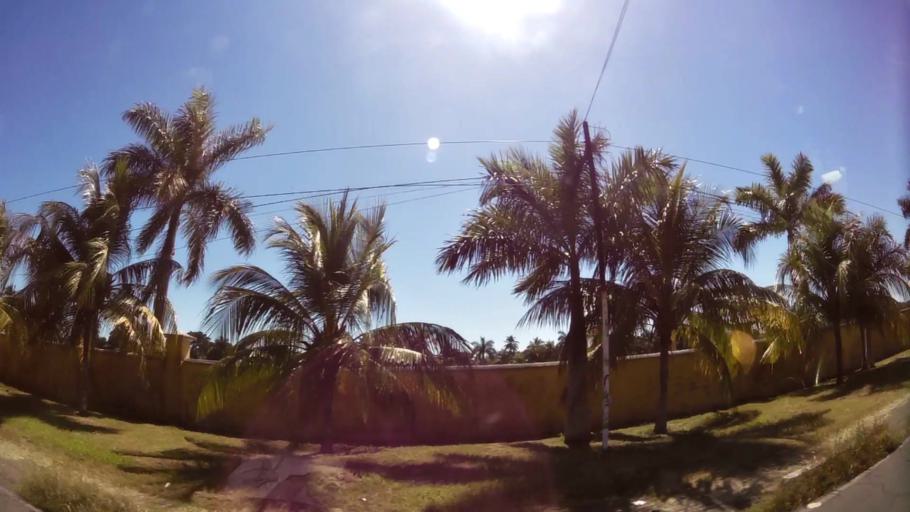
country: GT
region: Escuintla
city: Iztapa
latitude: 13.9392
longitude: -90.7209
